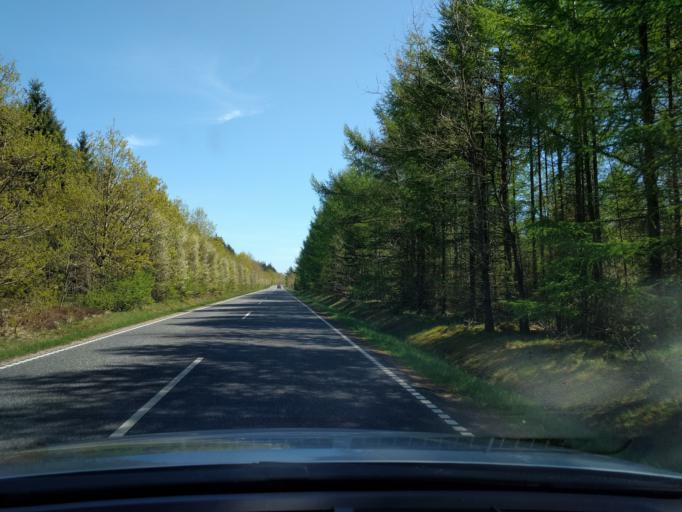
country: DK
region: South Denmark
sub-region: Billund Kommune
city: Grindsted
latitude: 55.6773
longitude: 8.9634
